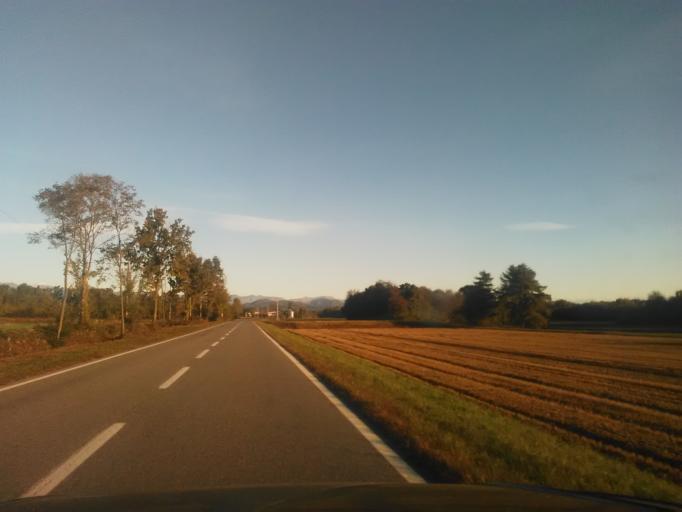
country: IT
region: Piedmont
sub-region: Provincia di Vercelli
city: Rovasenda
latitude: 45.5464
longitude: 8.3020
